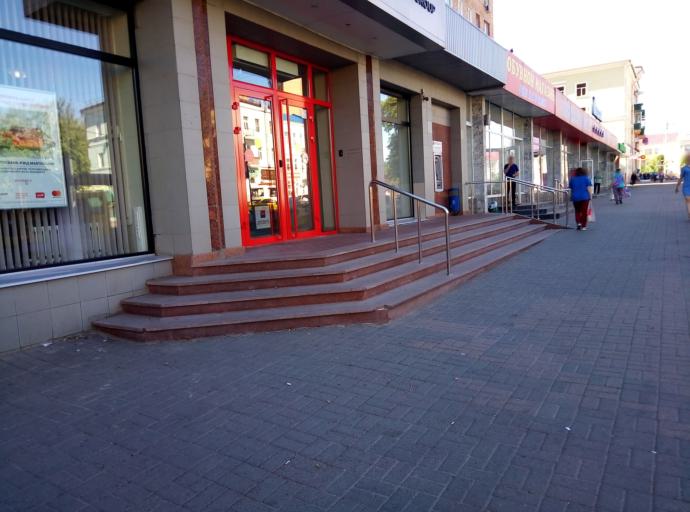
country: RU
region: Kursk
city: Kursk
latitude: 51.7468
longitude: 36.1943
